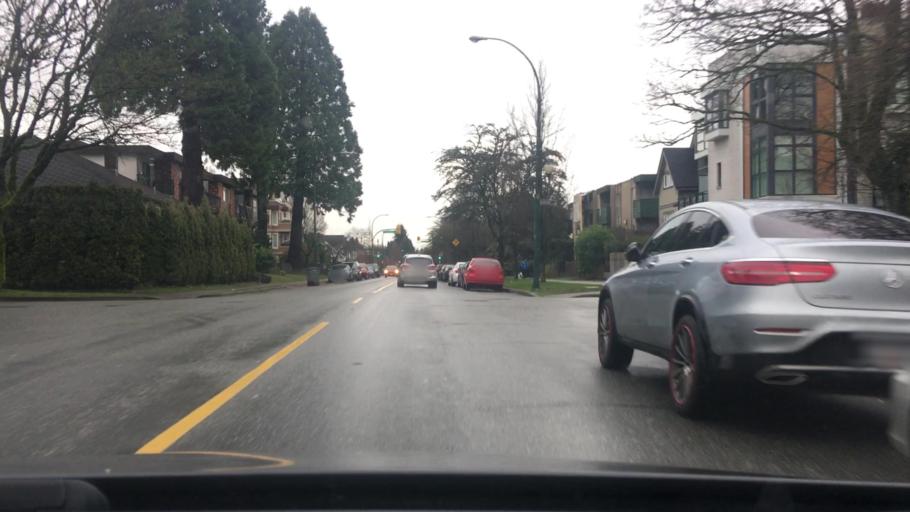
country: CA
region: British Columbia
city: Vancouver
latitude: 49.2567
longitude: -123.1029
